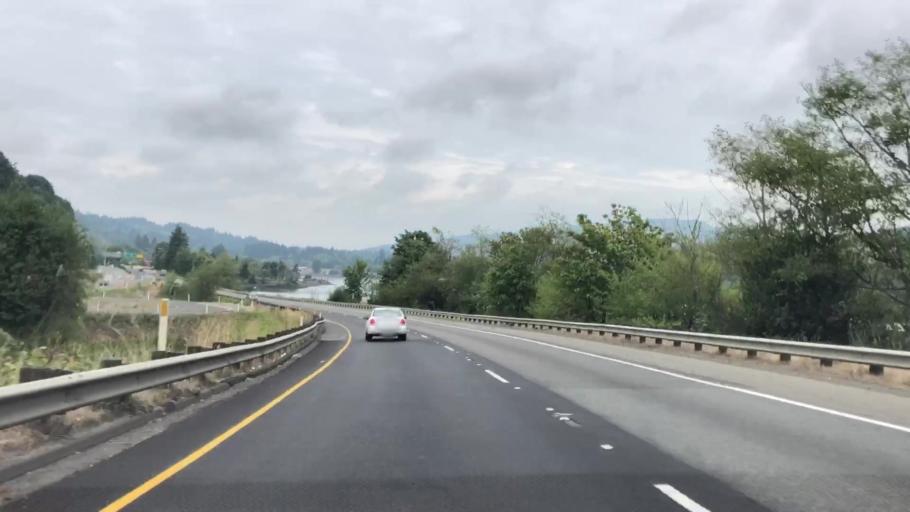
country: US
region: Washington
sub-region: Kitsap County
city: Navy Yard City
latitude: 47.5282
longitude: -122.6793
